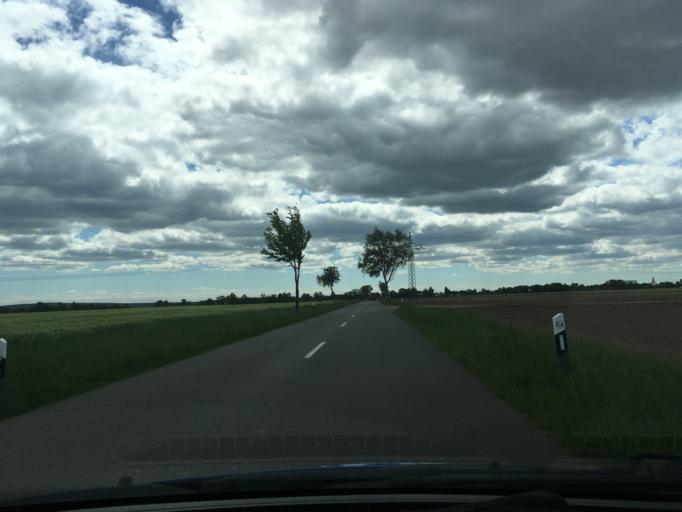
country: DE
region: Lower Saxony
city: Suderburg
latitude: 52.9183
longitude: 10.4391
